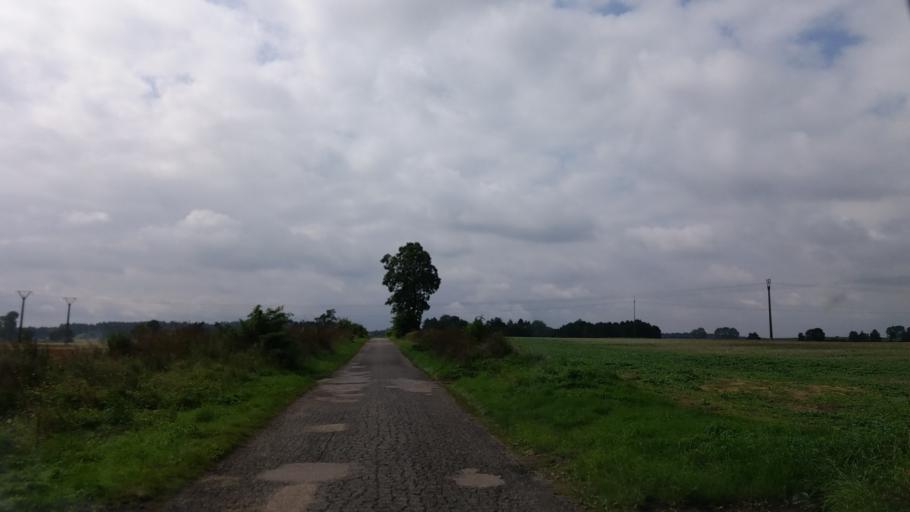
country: PL
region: West Pomeranian Voivodeship
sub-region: Powiat choszczenski
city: Krzecin
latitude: 53.0995
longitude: 15.4900
